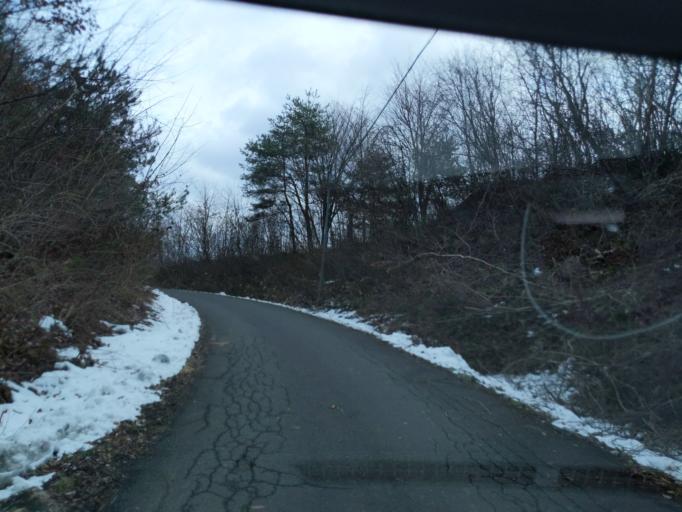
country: JP
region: Iwate
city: Ichinoseki
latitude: 38.9782
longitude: 141.0196
